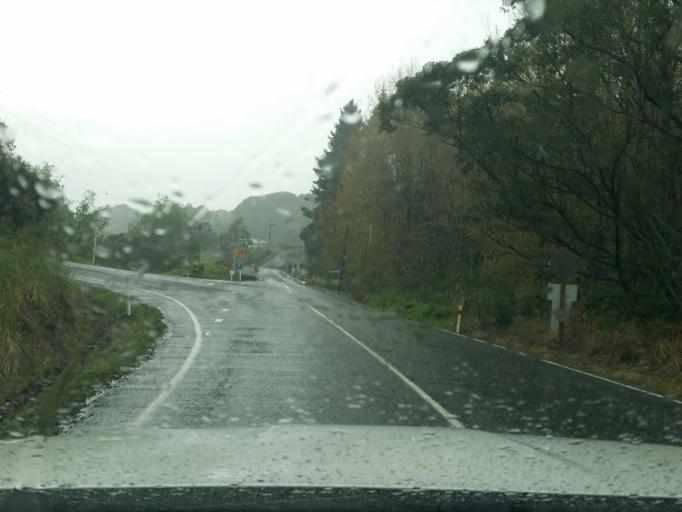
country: NZ
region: Northland
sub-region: Kaipara District
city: Dargaville
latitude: -35.7840
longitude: 173.9614
